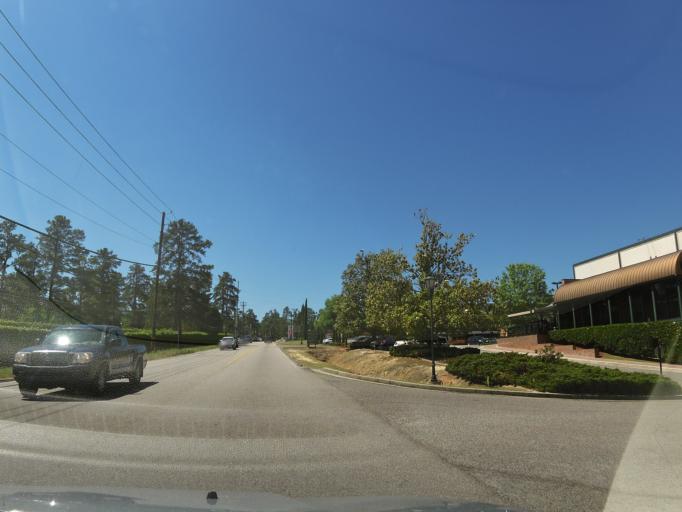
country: US
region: Georgia
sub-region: Columbia County
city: Martinez
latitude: 33.4873
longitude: -82.0295
